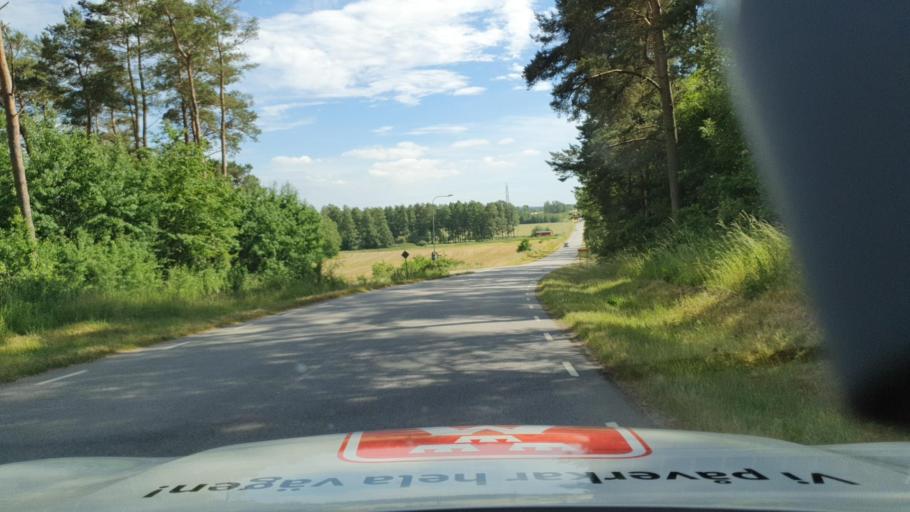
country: SE
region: Skane
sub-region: Sjobo Kommun
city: Sjoebo
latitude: 55.6311
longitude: 13.6572
